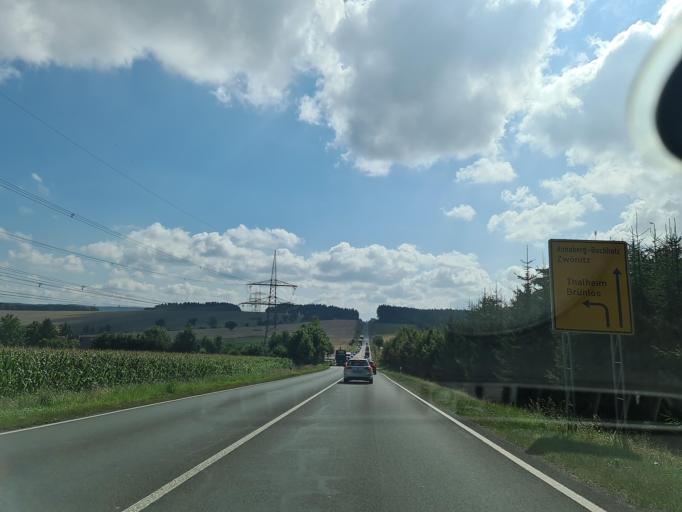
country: DE
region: Saxony
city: Stollberg
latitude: 50.6861
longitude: 12.7996
